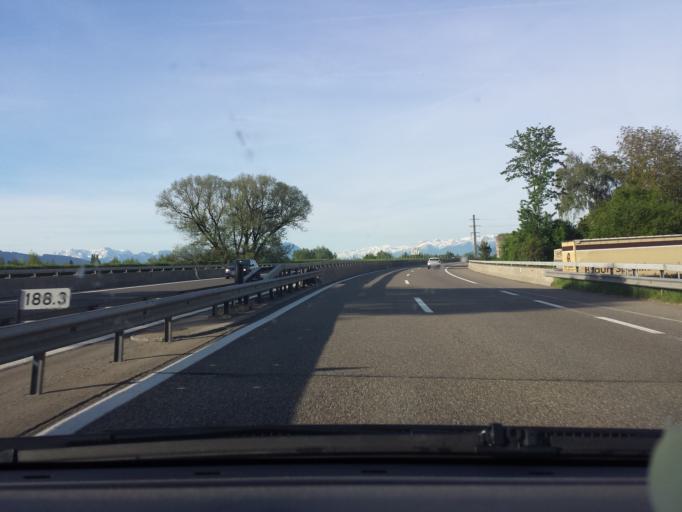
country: CH
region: Saint Gallen
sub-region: Wahlkreis Rheintal
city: Sankt Margrethen
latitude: 47.4467
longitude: 9.6534
